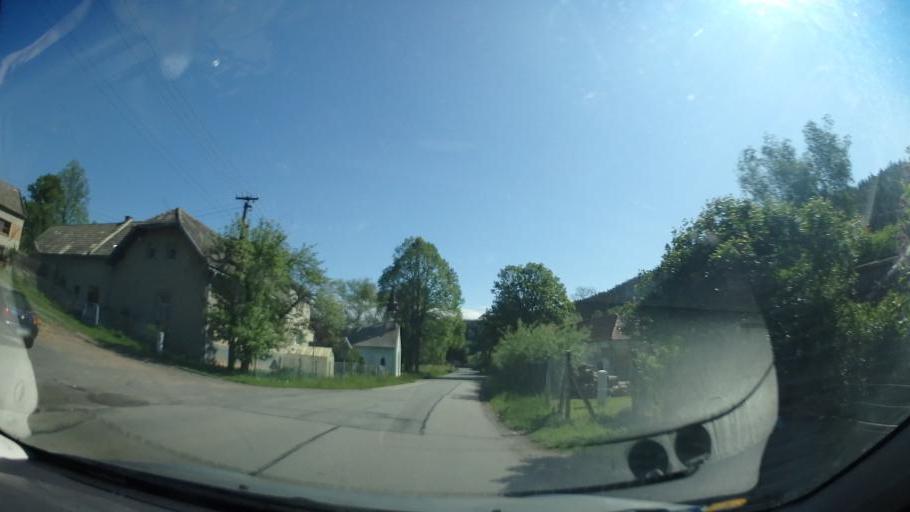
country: CZ
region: South Moravian
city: Velke Opatovice
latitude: 49.6612
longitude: 16.6305
